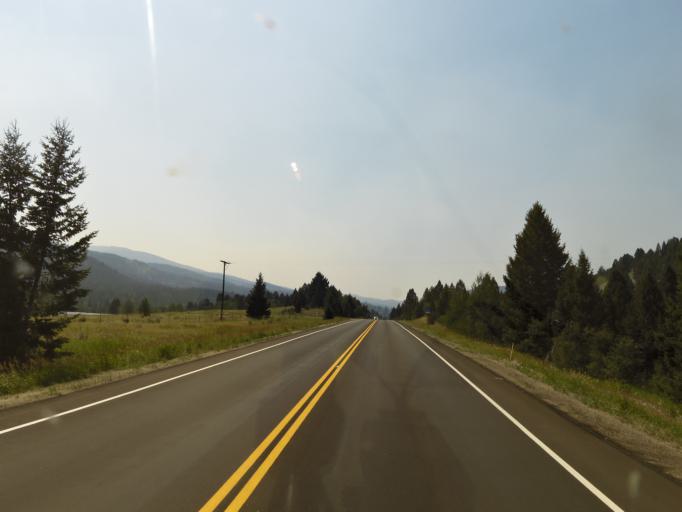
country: US
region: Montana
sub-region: Deer Lodge County
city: Anaconda
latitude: 46.1627
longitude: -113.0950
